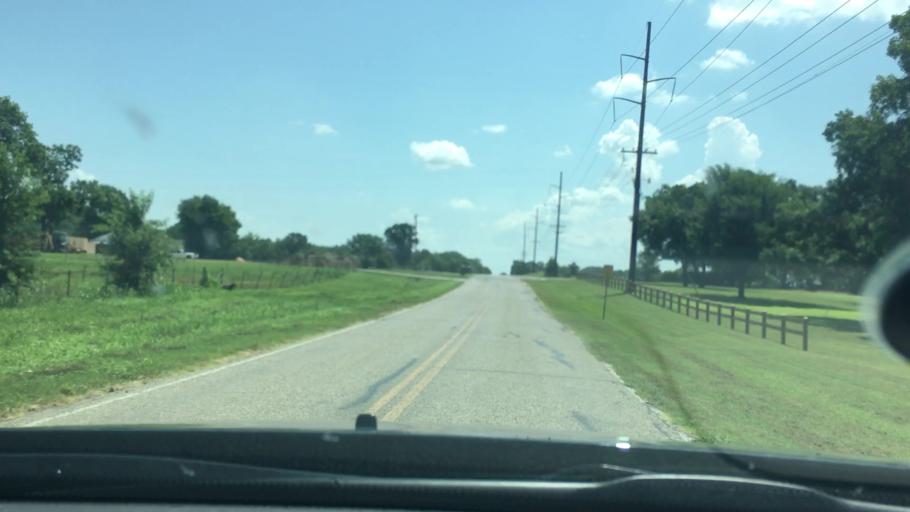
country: US
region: Oklahoma
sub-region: Pontotoc County
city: Ada
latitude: 34.6945
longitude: -96.5756
